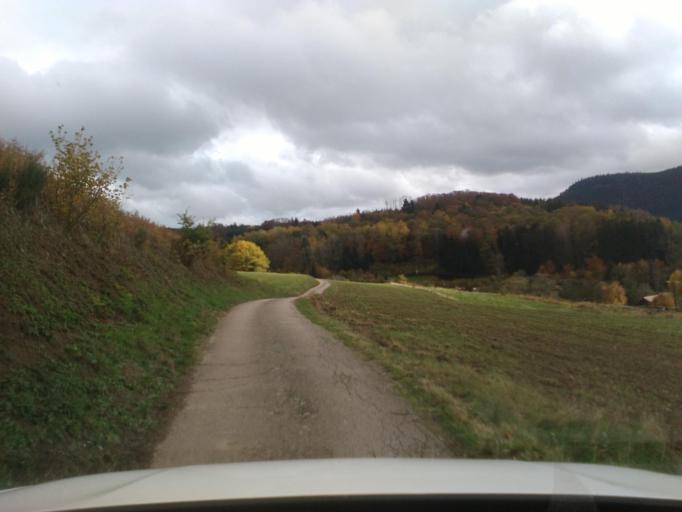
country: FR
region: Lorraine
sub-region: Departement des Vosges
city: Senones
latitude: 48.3370
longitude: 7.0185
